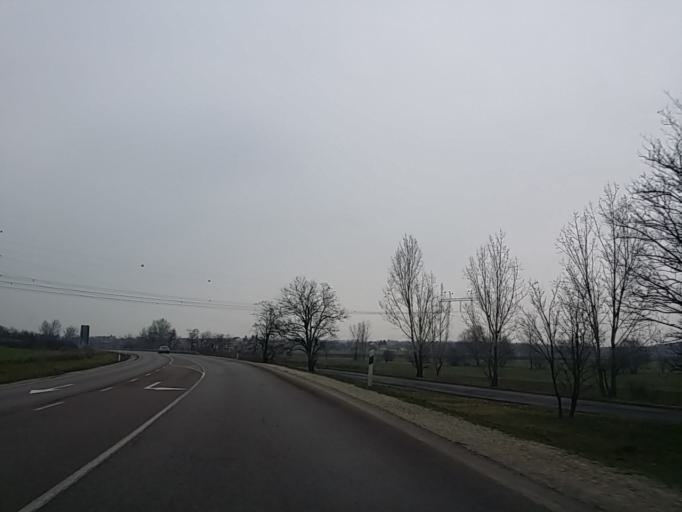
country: HU
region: Borsod-Abauj-Zemplen
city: Mezokeresztes
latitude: 47.8728
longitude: 20.6792
